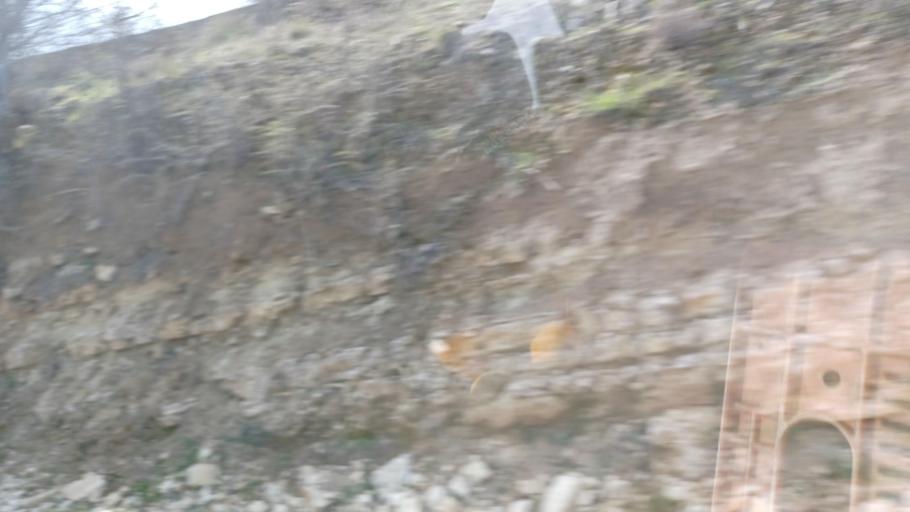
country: CY
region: Limassol
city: Pachna
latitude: 34.7882
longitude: 32.7371
